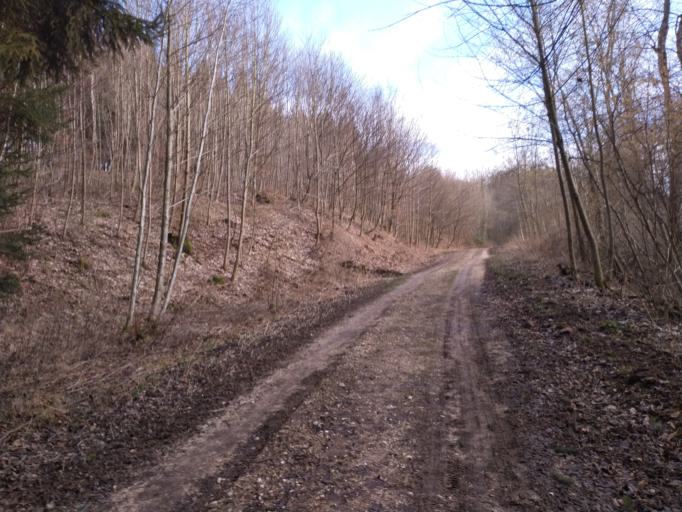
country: DE
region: Bavaria
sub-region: Swabia
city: Guenzburg
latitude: 48.4338
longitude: 10.3150
